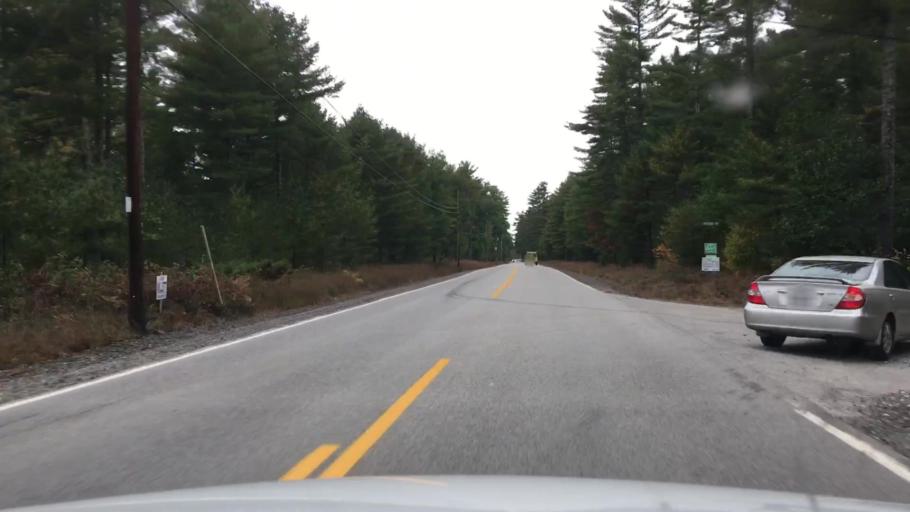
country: US
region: Maine
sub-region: Cumberland County
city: Harrison
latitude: 44.2181
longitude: -70.6882
